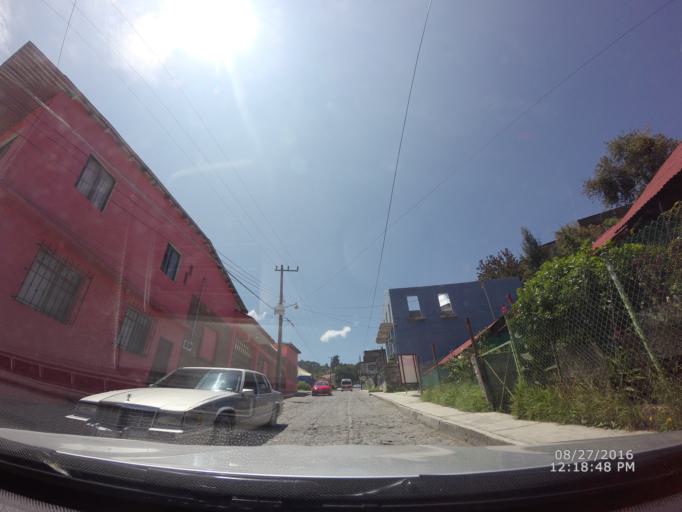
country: MX
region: Hidalgo
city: Mineral del Monte
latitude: 20.1372
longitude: -98.6707
